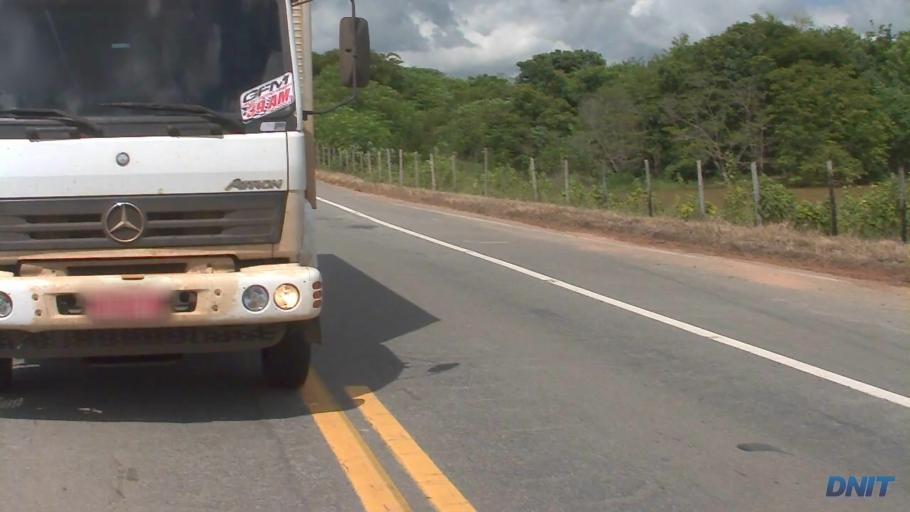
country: BR
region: Minas Gerais
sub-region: Governador Valadares
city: Governador Valadares
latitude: -19.0499
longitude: -42.1573
